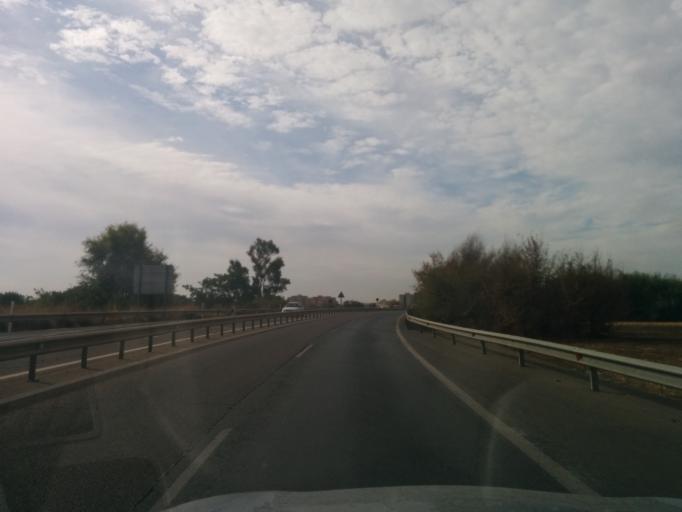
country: ES
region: Andalusia
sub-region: Provincia de Sevilla
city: Sevilla
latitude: 37.4327
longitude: -5.9656
